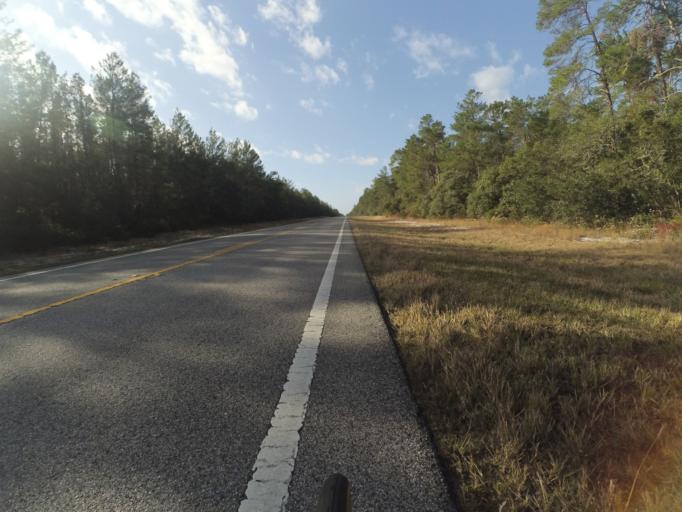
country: US
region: Florida
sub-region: Lake County
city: Astor
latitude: 29.1275
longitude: -81.6093
